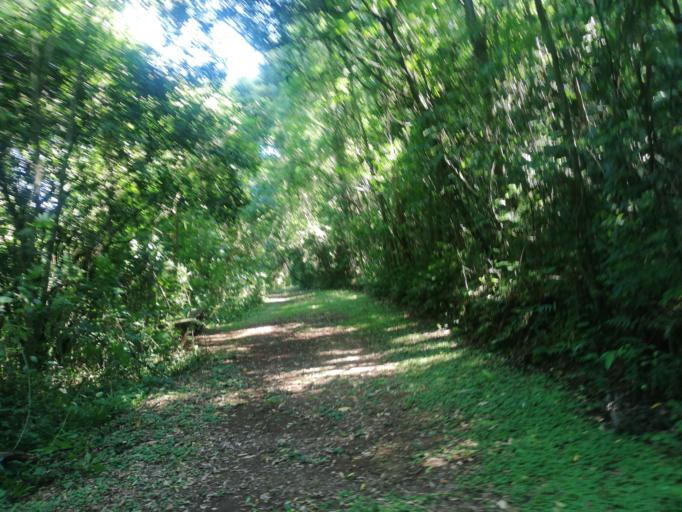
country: AR
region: Misiones
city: Cerro Azul
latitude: -27.7471
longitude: -55.5606
